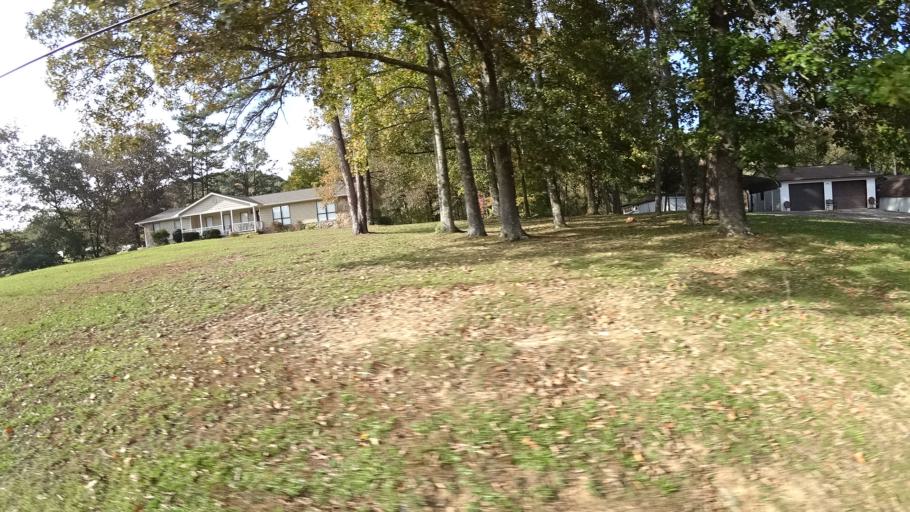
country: US
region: Tennessee
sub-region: Knox County
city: Farragut
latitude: 35.9174
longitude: -84.1804
